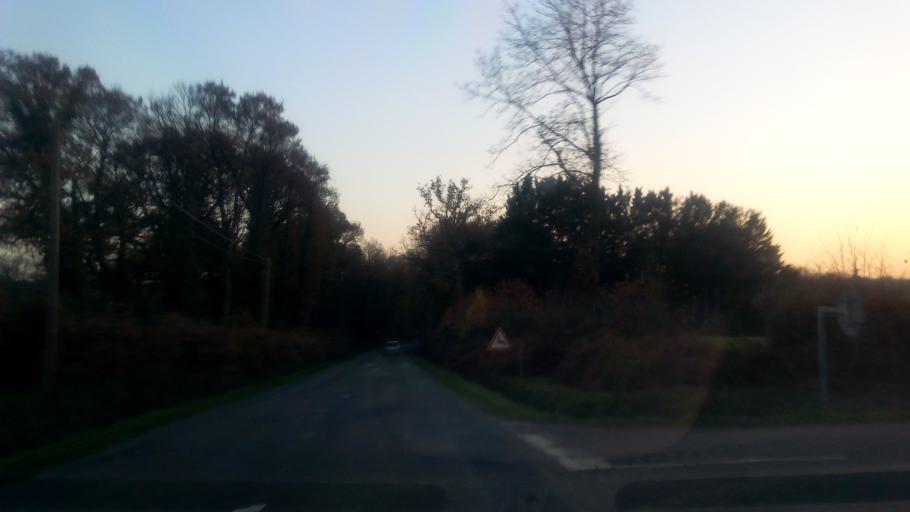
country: FR
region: Brittany
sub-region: Departement d'Ille-et-Vilaine
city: Bains-sur-Oust
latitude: 47.7179
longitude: -2.0539
